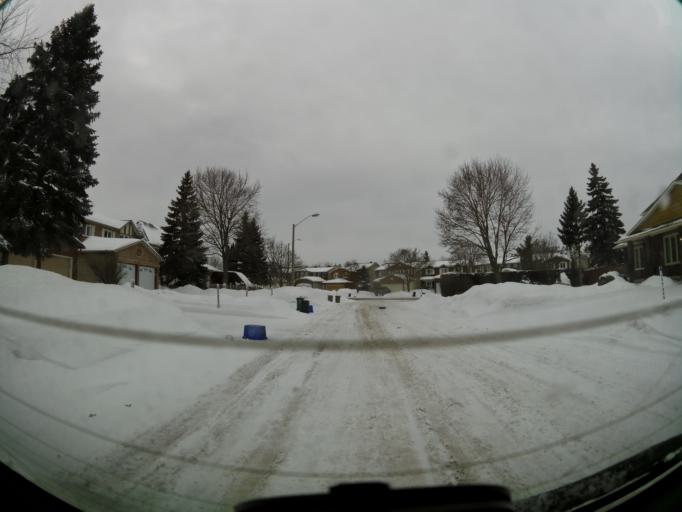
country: CA
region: Ontario
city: Ottawa
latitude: 45.3721
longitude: -75.6130
